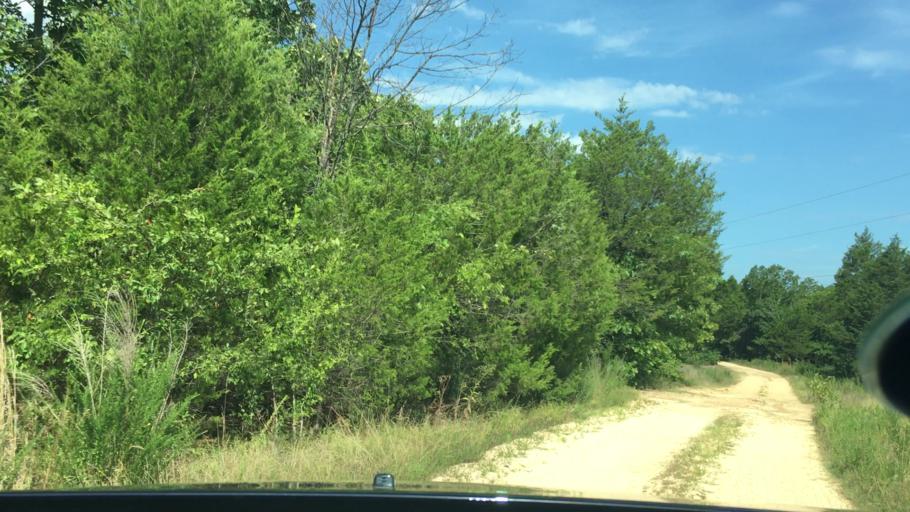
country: US
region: Oklahoma
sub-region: Pontotoc County
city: Ada
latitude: 34.7653
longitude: -96.5539
